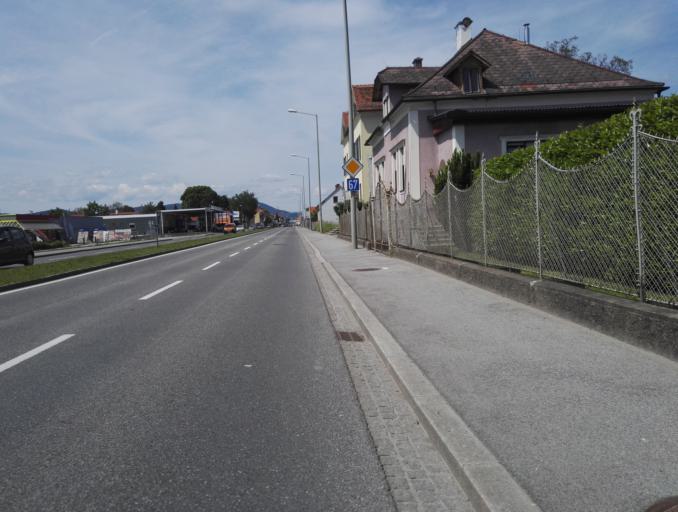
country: AT
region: Styria
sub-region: Politischer Bezirk Graz-Umgebung
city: Feldkirchen bei Graz
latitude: 47.0214
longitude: 15.4375
